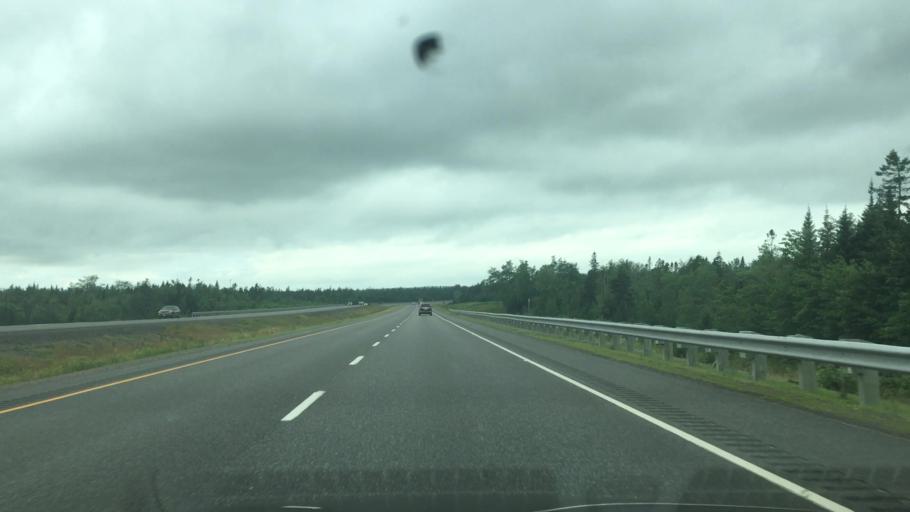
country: CA
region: Nova Scotia
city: Truro
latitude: 45.4312
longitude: -63.5629
